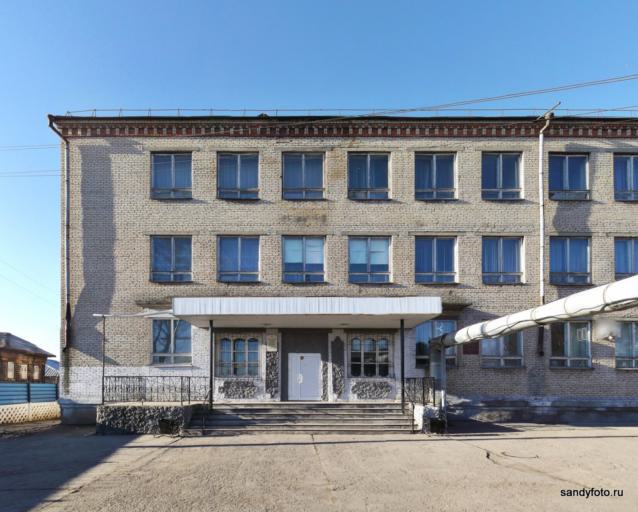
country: RU
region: Chelyabinsk
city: Troitsk
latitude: 54.0944
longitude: 61.5736
